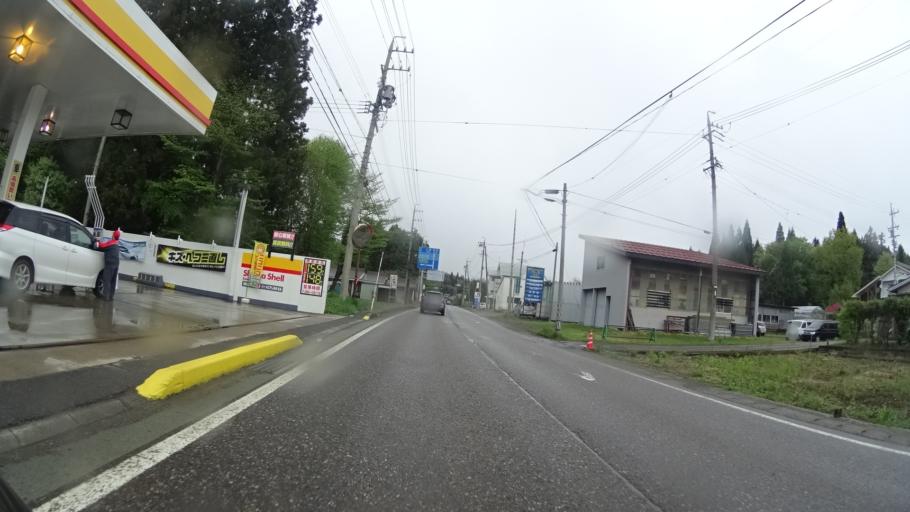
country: JP
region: Nagano
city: Nagano-shi
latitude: 36.8146
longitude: 138.1975
